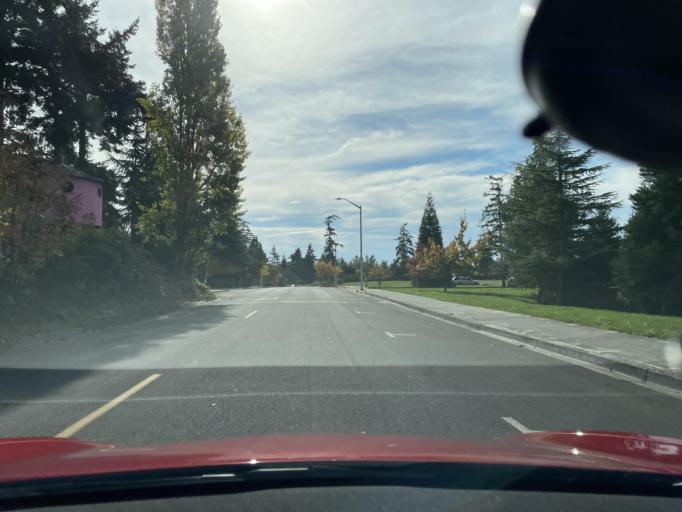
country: US
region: Washington
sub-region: San Juan County
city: Friday Harbor
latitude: 48.5310
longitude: -123.0192
